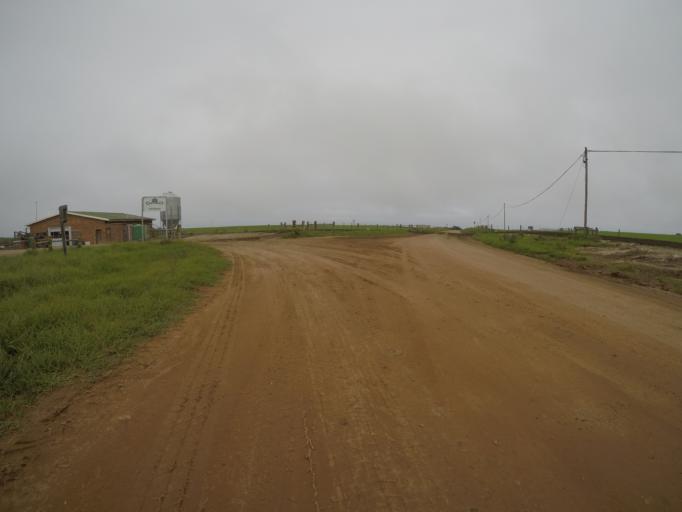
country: ZA
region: Eastern Cape
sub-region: Cacadu District Municipality
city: Kareedouw
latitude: -34.0685
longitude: 24.2386
